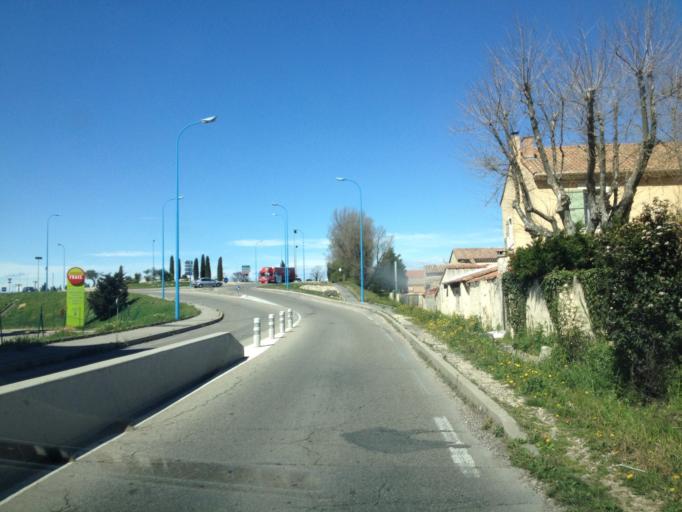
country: FR
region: Provence-Alpes-Cote d'Azur
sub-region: Departement du Vaucluse
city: Le Pontet
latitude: 43.9723
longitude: 4.8676
